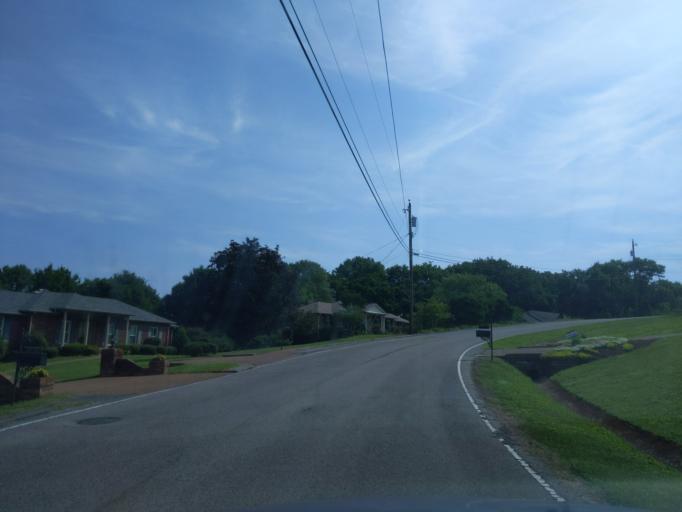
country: US
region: Tennessee
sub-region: Williamson County
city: Brentwood Estates
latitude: 36.0303
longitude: -86.7394
